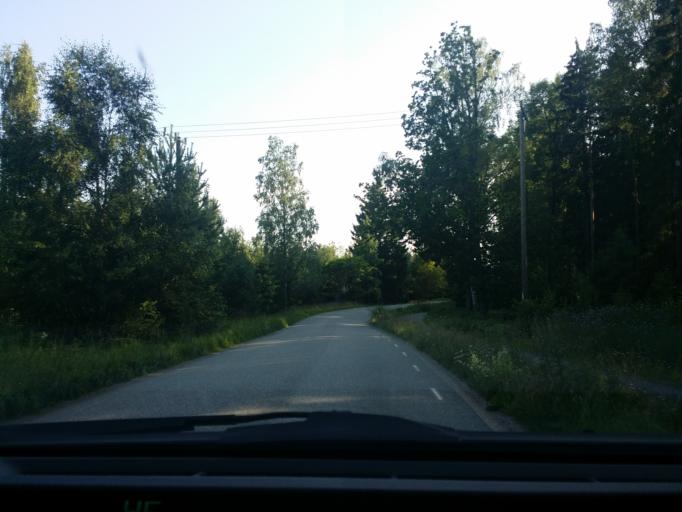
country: SE
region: Vaestmanland
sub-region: Vasteras
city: Tillberga
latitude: 59.5742
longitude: 16.6711
